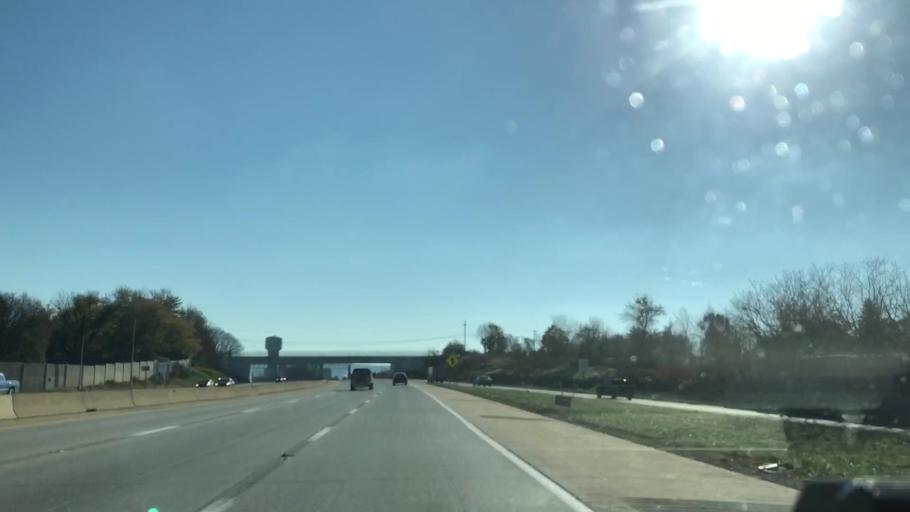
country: US
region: Pennsylvania
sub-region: Lehigh County
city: Wescosville
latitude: 40.5712
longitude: -75.5377
